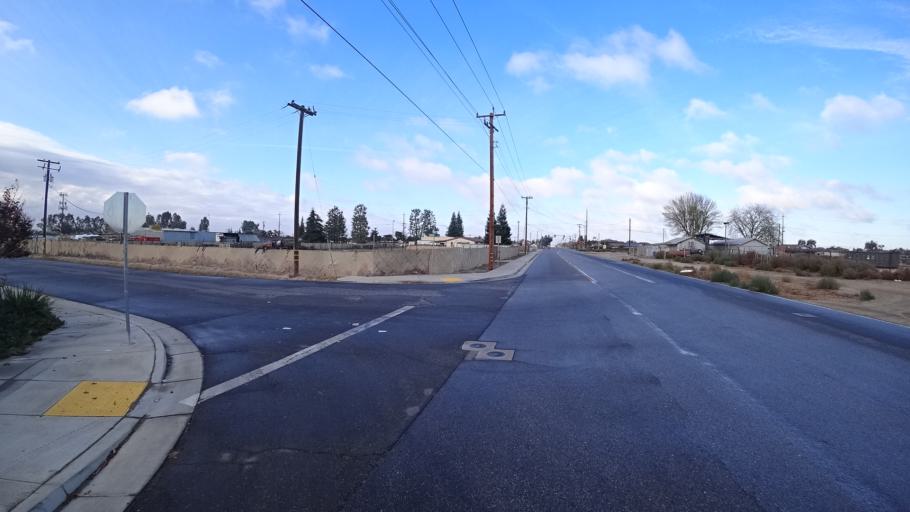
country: US
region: California
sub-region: Kern County
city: Greenfield
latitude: 35.2885
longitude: -119.0008
